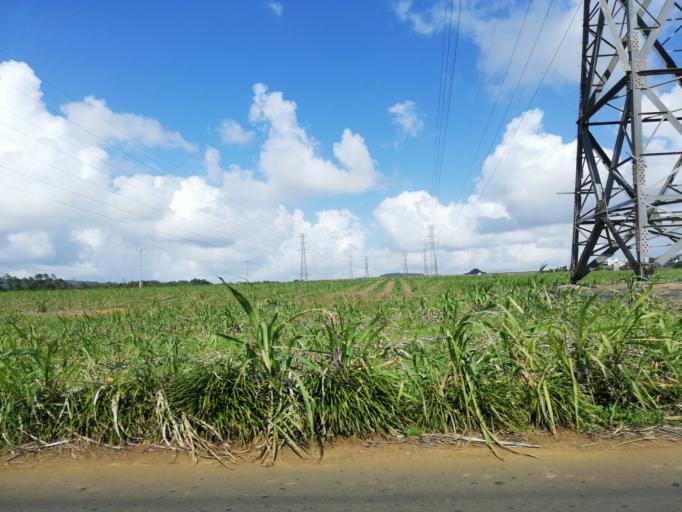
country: MU
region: Moka
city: Verdun
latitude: -20.2142
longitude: 57.5536
